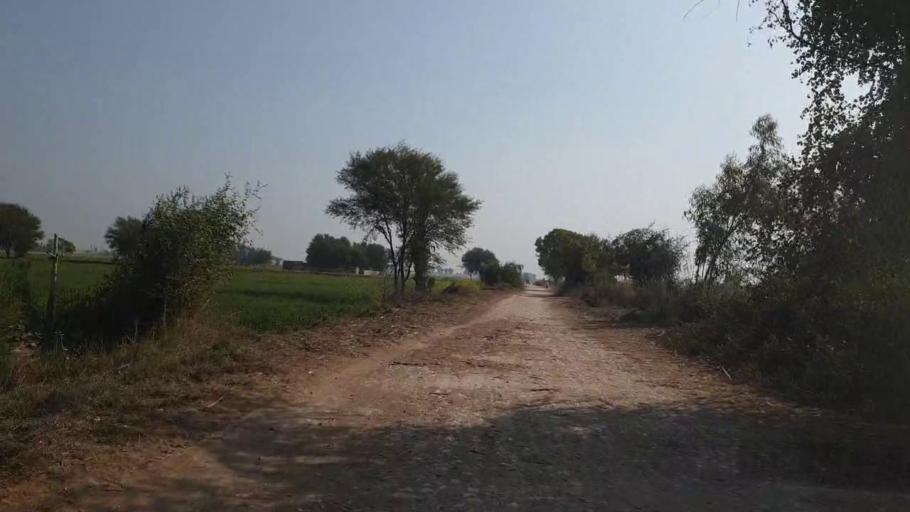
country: PK
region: Sindh
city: Bhit Shah
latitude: 25.7204
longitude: 68.5415
